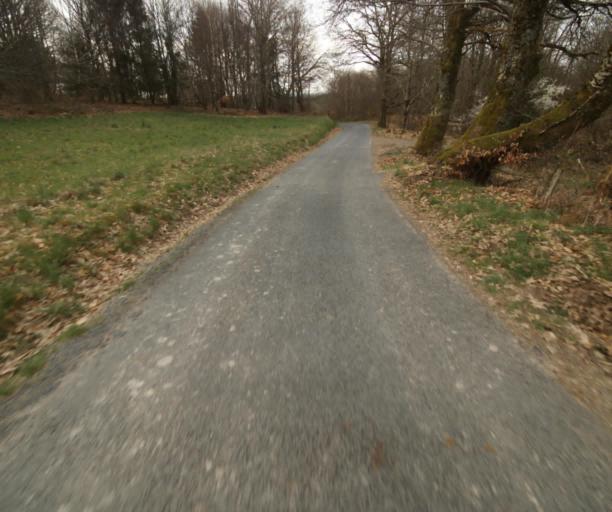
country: FR
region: Limousin
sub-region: Departement de la Correze
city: Correze
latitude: 45.4410
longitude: 1.8220
